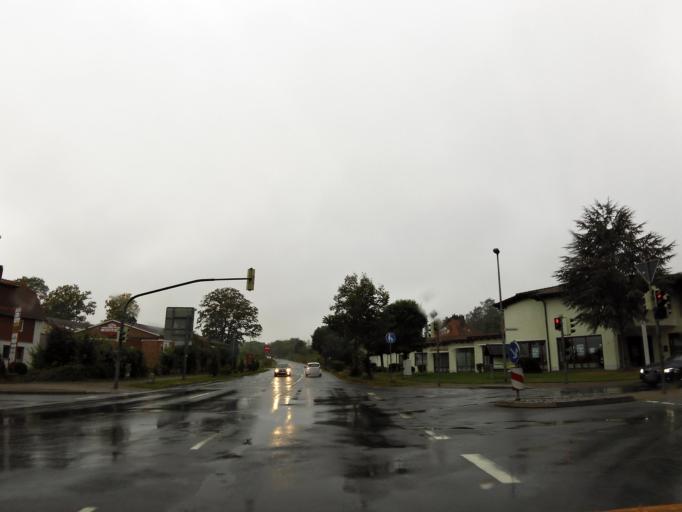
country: DE
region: Lower Saxony
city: Bad Sachsa
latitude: 51.5916
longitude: 10.5666
